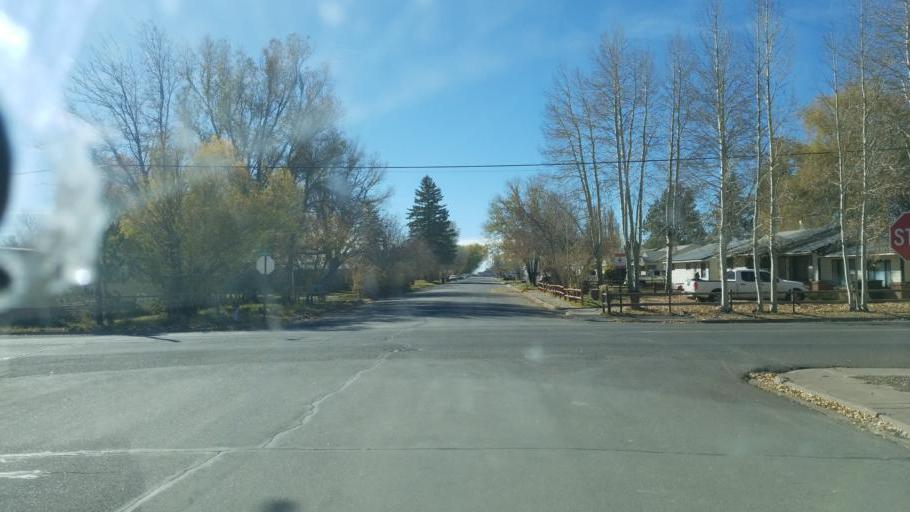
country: US
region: Colorado
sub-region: Rio Grande County
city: Monte Vista
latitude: 37.5747
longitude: -106.1468
